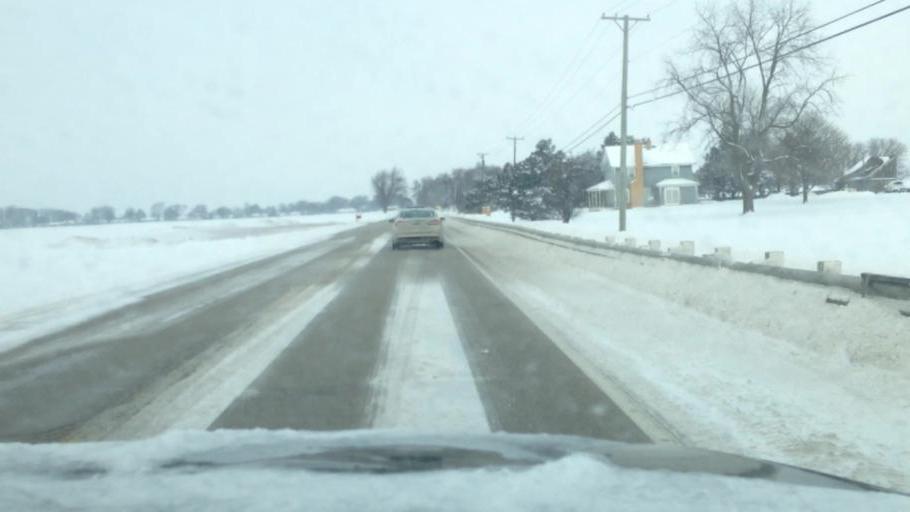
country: US
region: Illinois
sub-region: McHenry County
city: Hebron
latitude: 42.4556
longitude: -88.4329
